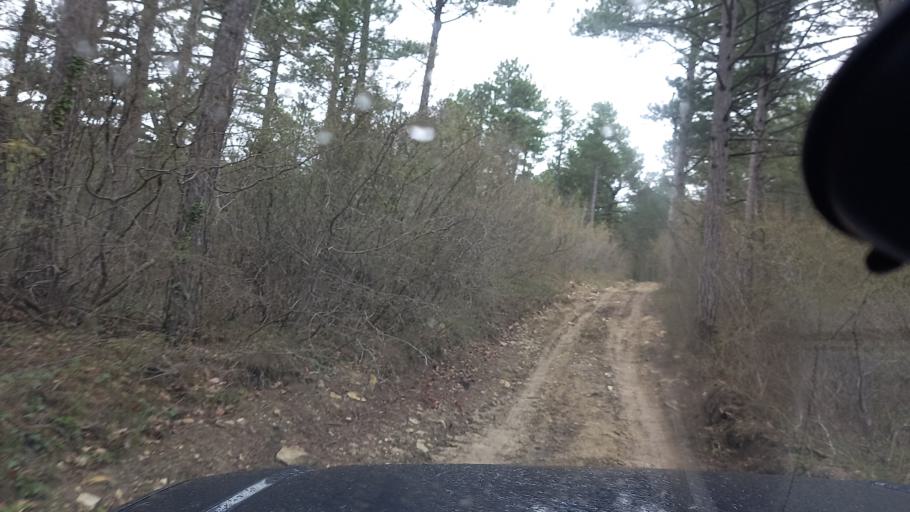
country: RU
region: Krasnodarskiy
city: Arkhipo-Osipovka
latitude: 44.3736
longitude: 38.4732
